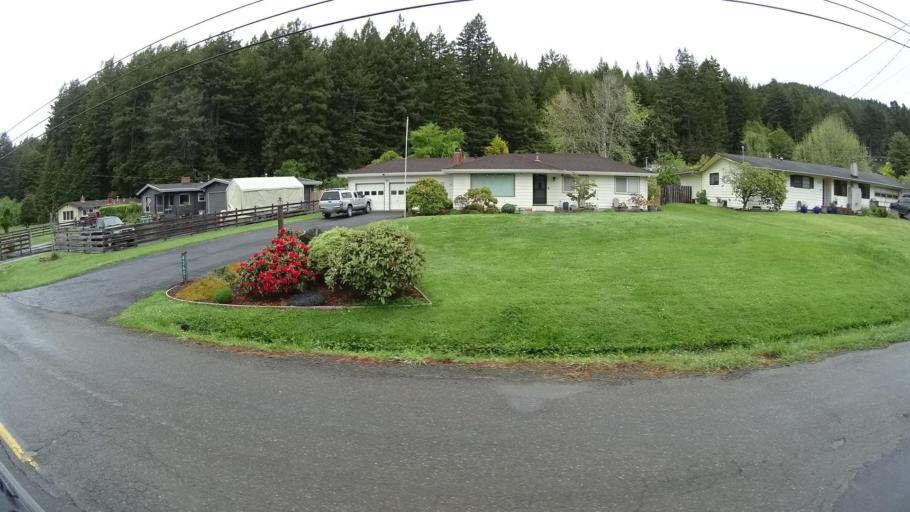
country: US
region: California
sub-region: Humboldt County
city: Bayside
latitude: 40.8323
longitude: -124.0428
